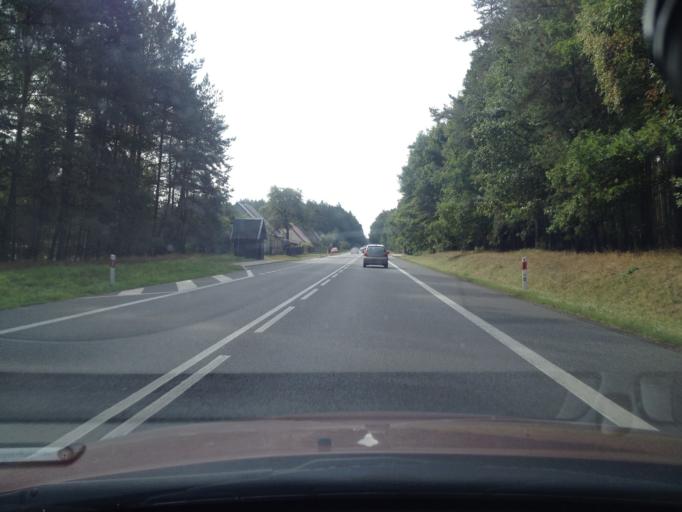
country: PL
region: West Pomeranian Voivodeship
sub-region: Powiat goleniowski
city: Przybiernow
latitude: 53.7370
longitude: 14.7749
